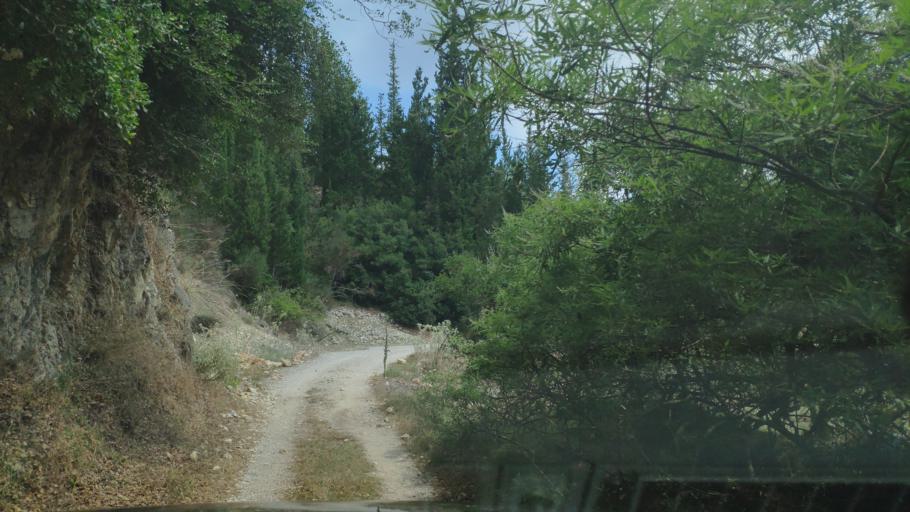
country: GR
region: Ionian Islands
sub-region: Lefkada
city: Lefkada
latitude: 38.8001
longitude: 20.6721
